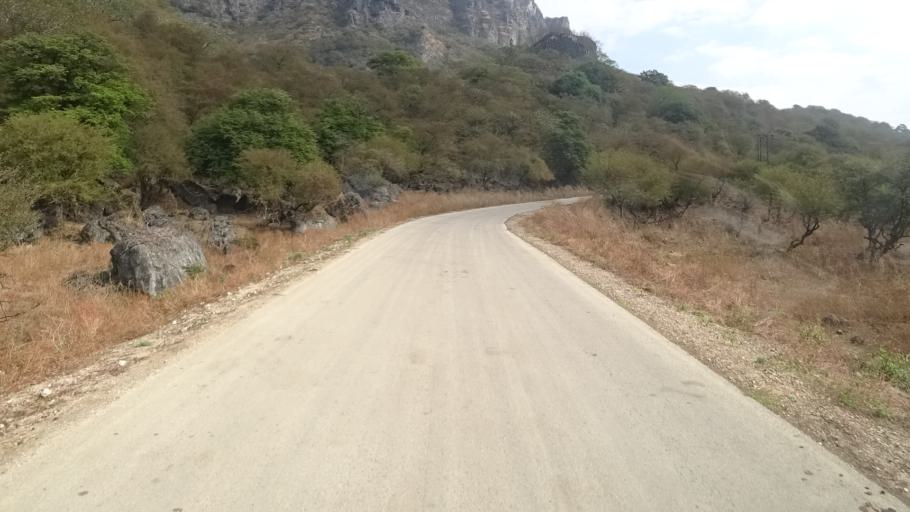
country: YE
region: Al Mahrah
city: Hawf
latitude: 16.7116
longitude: 53.2291
